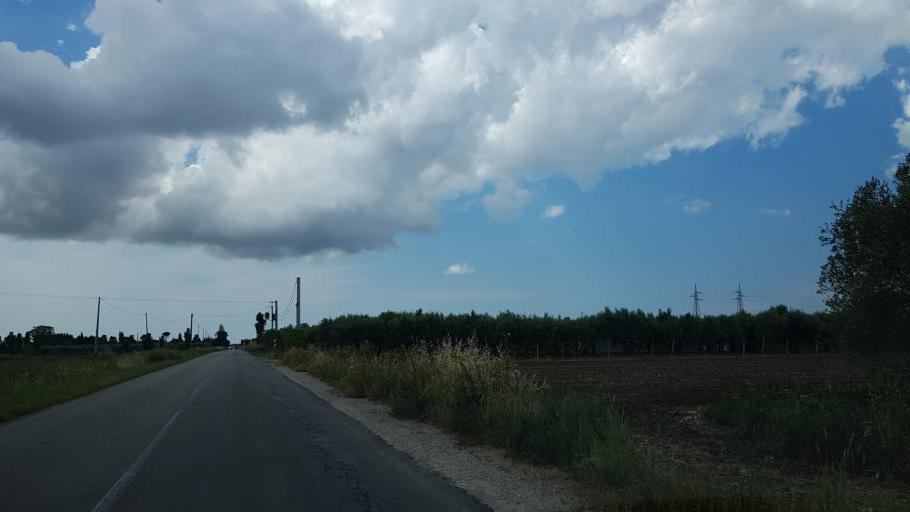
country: IT
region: Apulia
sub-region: Provincia di Brindisi
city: San Pancrazio Salentino
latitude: 40.3917
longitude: 17.8352
